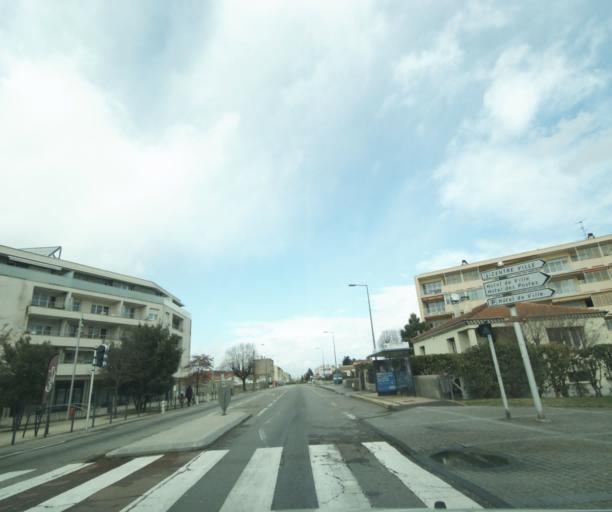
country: FR
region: Rhone-Alpes
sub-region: Departement de la Drome
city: Valence
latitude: 44.9466
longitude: 4.8934
